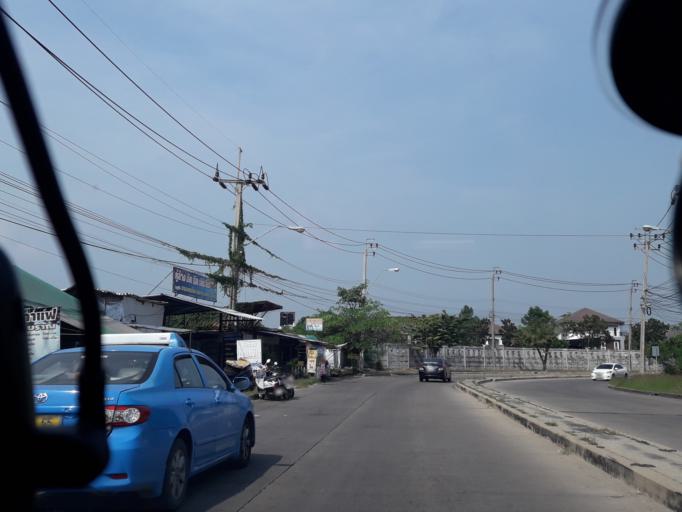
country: TH
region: Bangkok
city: Khan Na Yao
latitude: 13.8517
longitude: 100.7010
